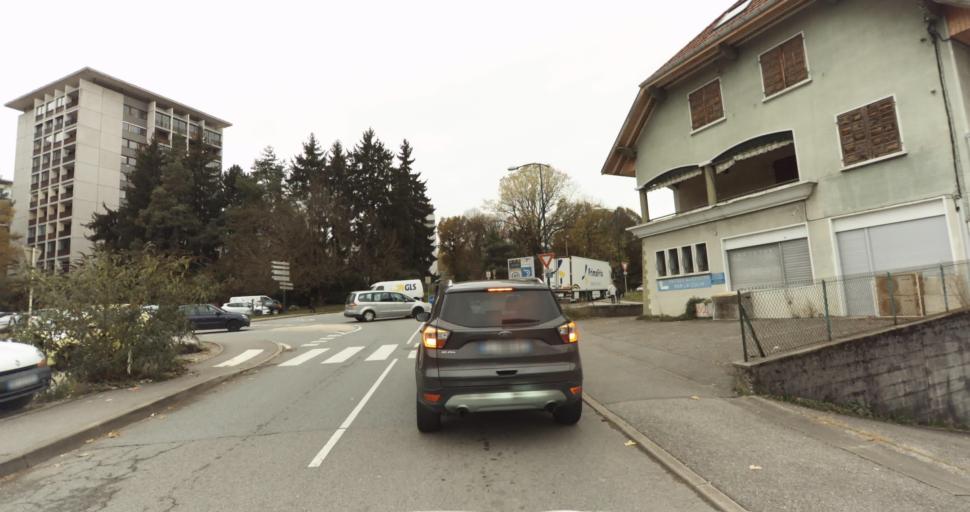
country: FR
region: Rhone-Alpes
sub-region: Departement de la Haute-Savoie
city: Annecy
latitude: 45.8948
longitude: 6.1138
